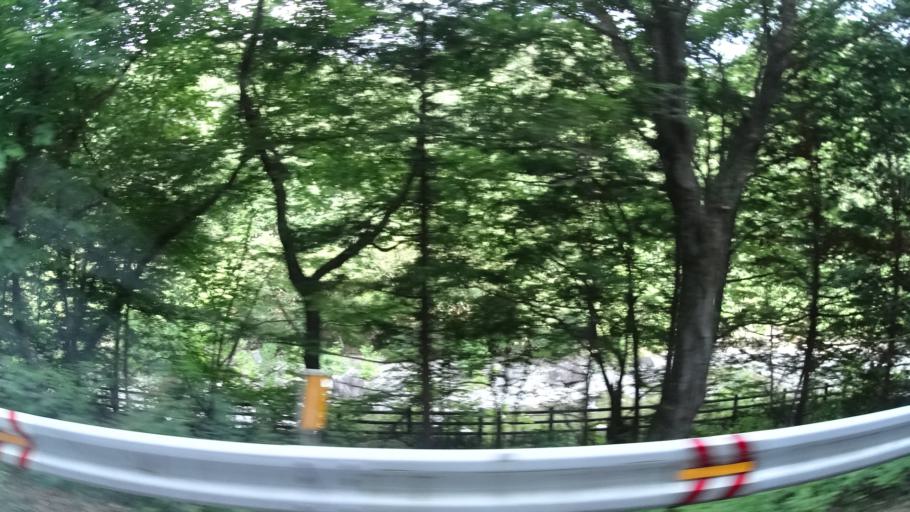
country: JP
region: Tochigi
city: Nikko
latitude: 36.6873
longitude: 139.4979
